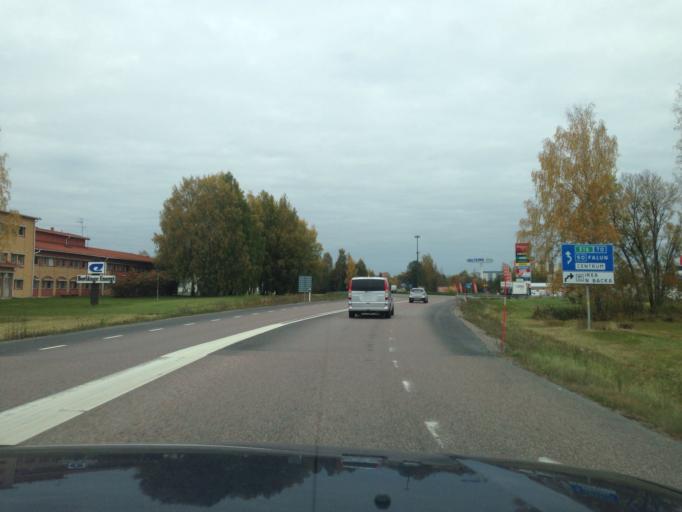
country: SE
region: Dalarna
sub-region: Borlange Kommun
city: Borlaenge
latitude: 60.4781
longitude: 15.4095
